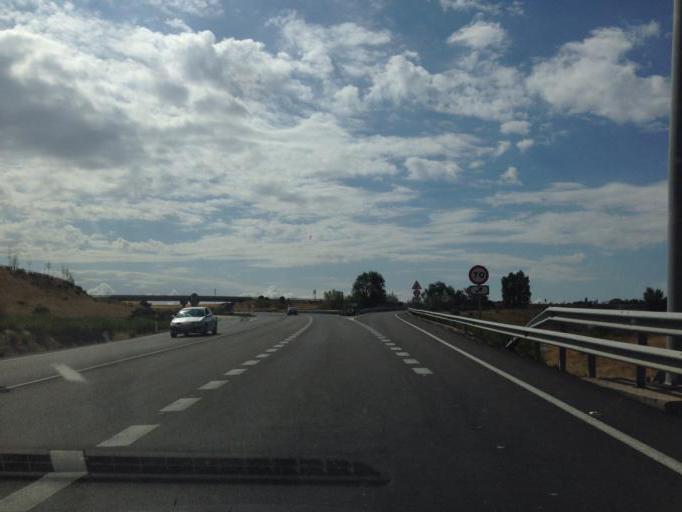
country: ES
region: Madrid
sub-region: Provincia de Madrid
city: Cobena
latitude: 40.5623
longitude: -3.5168
